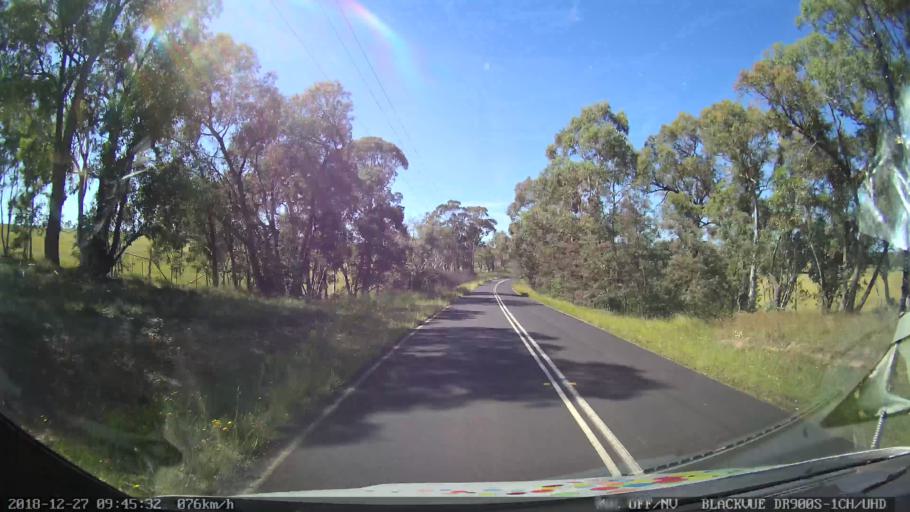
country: AU
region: New South Wales
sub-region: Lithgow
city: Portland
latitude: -33.3256
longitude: 149.9844
